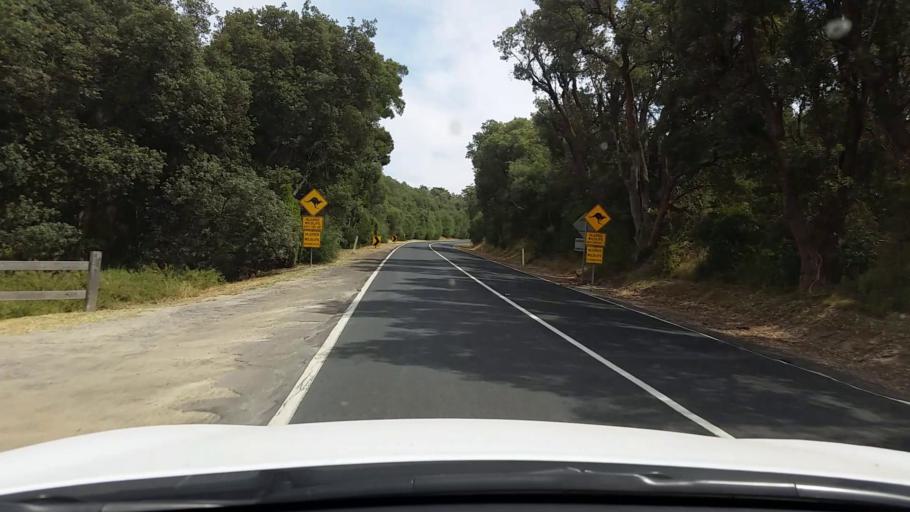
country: AU
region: Victoria
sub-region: Mornington Peninsula
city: Saint Andrews Beach
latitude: -38.4732
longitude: 144.9275
